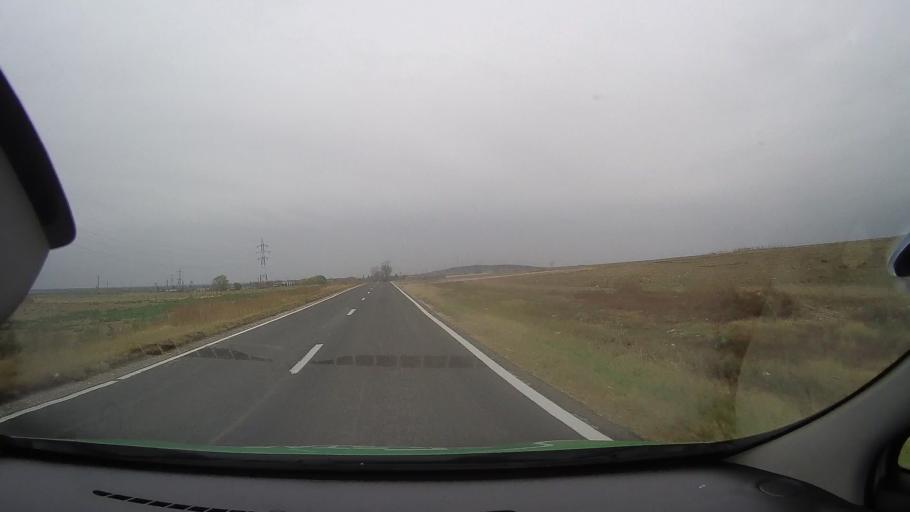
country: RO
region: Constanta
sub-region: Comuna Ciobanu
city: Ciobanu
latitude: 44.6934
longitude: 27.9754
